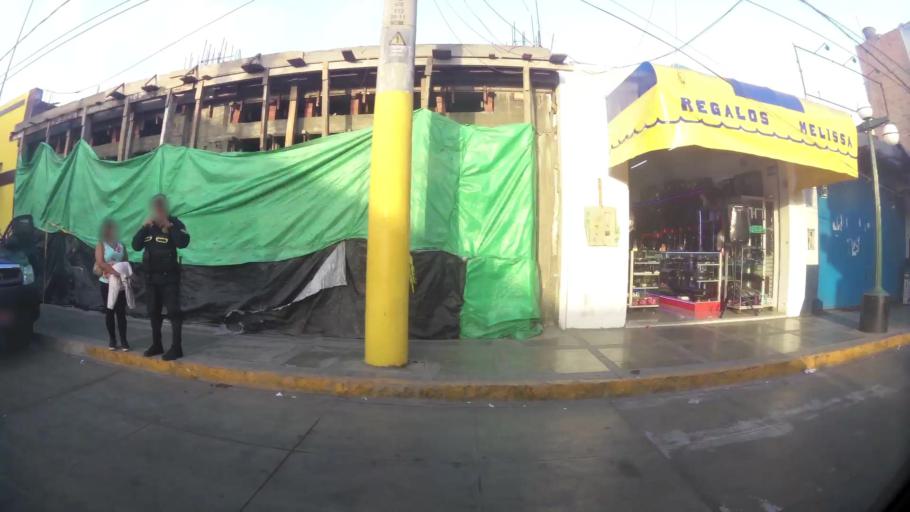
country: PE
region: Lima
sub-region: Huaura
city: Huacho
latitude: -11.1068
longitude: -77.6090
